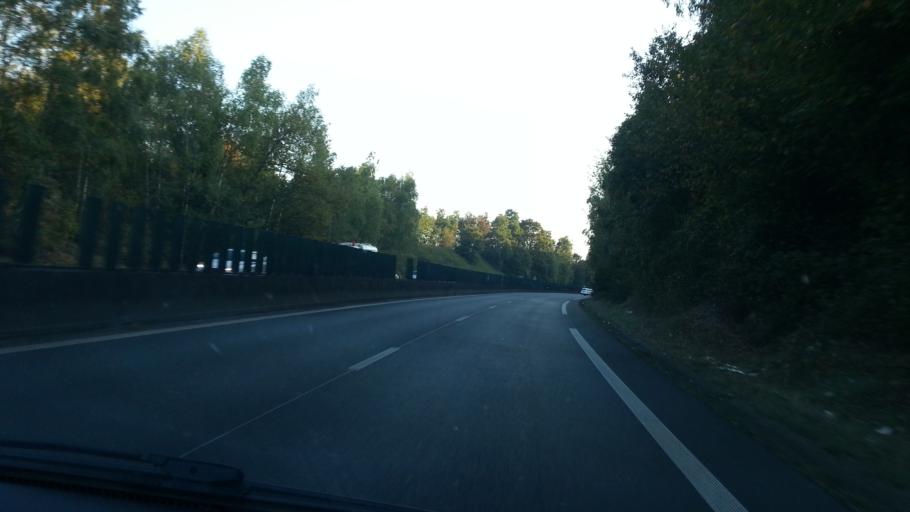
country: FR
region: Picardie
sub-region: Departement de l'Oise
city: Creil
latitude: 49.2579
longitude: 2.4921
